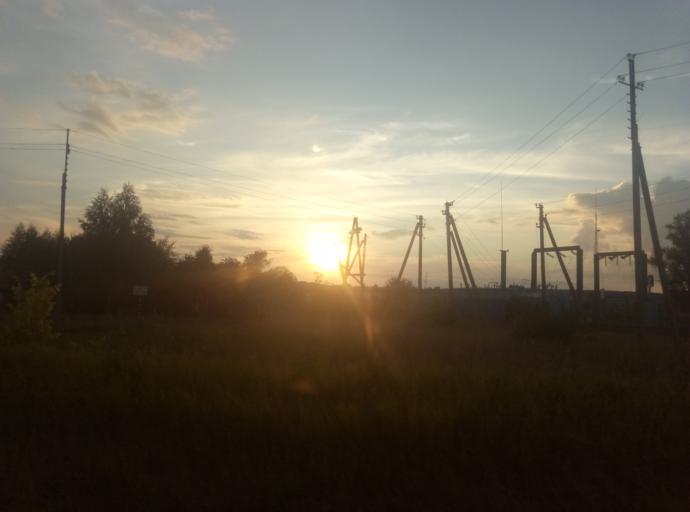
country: RU
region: Tula
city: Kireyevsk
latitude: 53.7998
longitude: 37.8636
